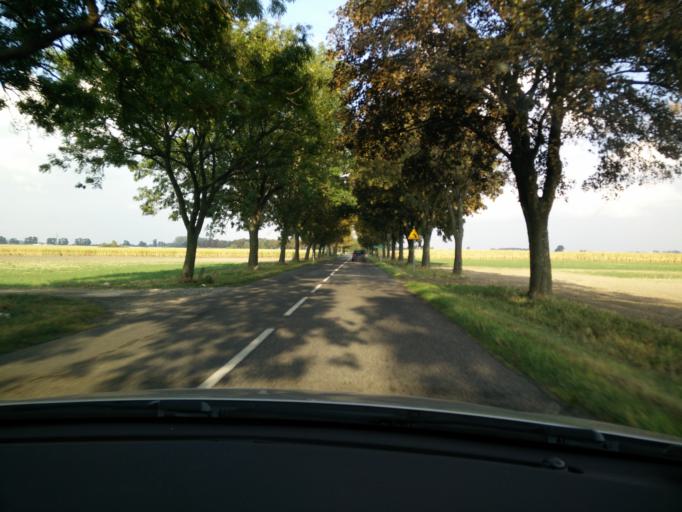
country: PL
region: Greater Poland Voivodeship
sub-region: Powiat sredzki
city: Dominowo
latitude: 52.2550
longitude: 17.4099
